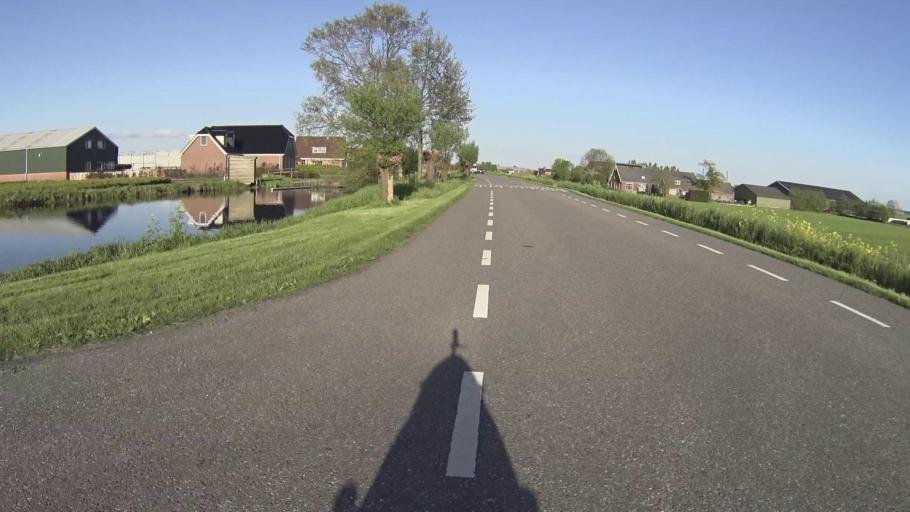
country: NL
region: South Holland
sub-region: Gemeente Rijnwoude
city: Benthuizen
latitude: 52.1046
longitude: 4.5391
